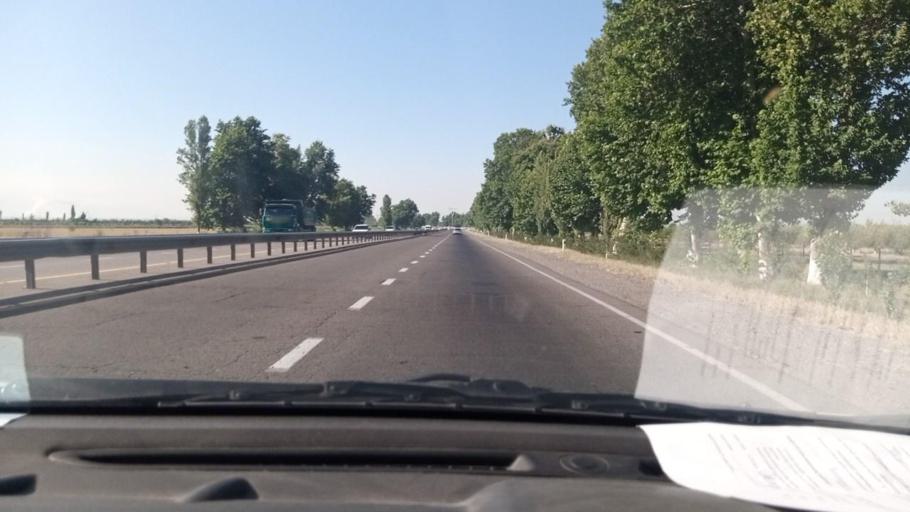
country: UZ
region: Toshkent Shahri
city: Bektemir
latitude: 41.1953
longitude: 69.4030
